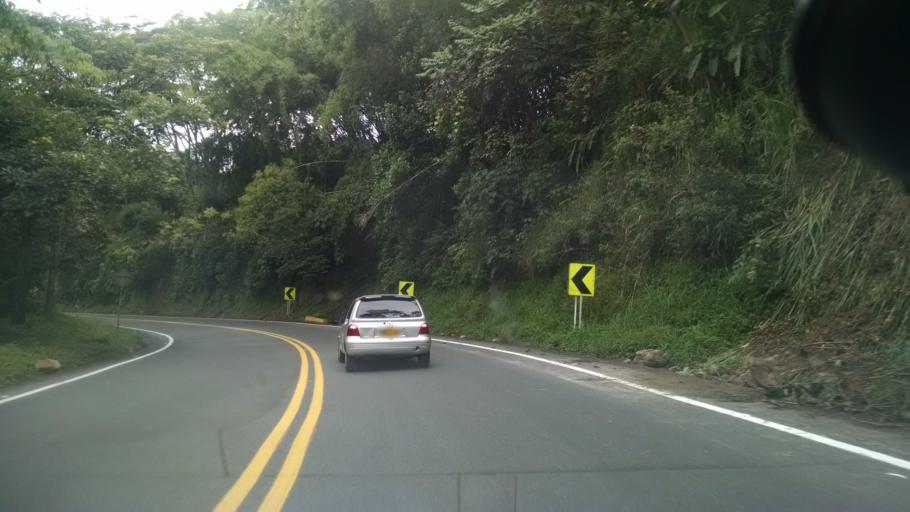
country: CO
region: Caldas
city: Palestina
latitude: 5.0386
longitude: -75.5979
